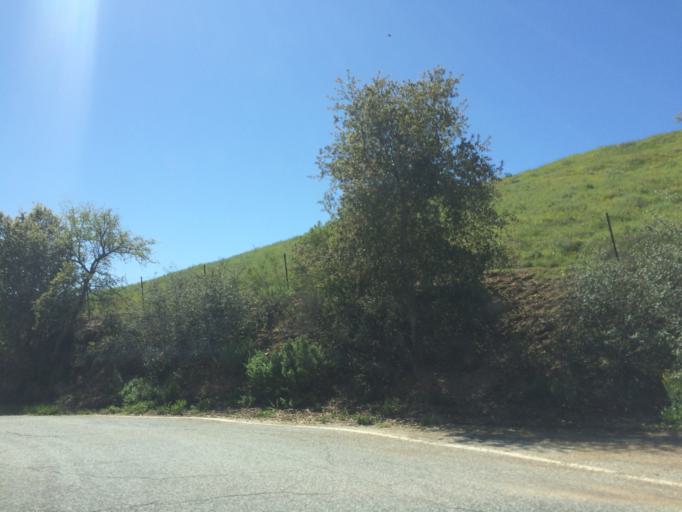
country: US
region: California
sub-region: Santa Clara County
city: Morgan Hill
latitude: 37.1745
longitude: -121.5690
